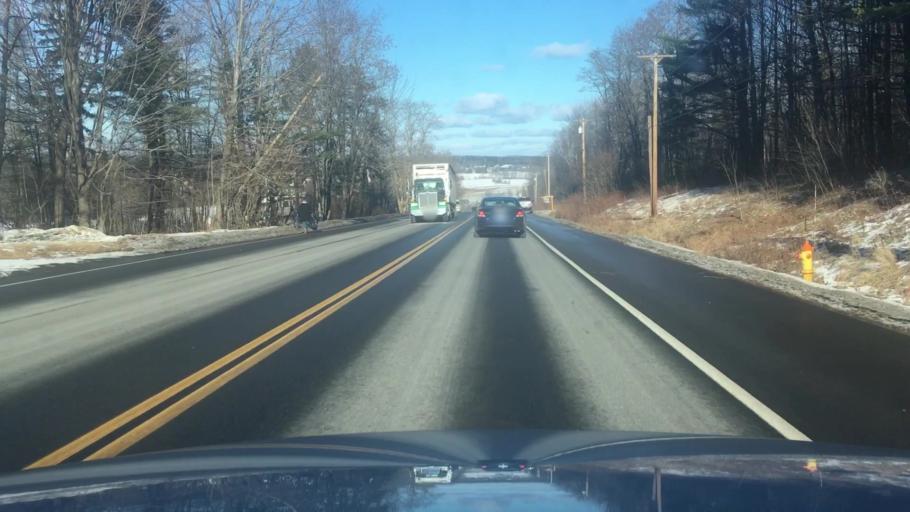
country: US
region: Maine
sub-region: Kennebec County
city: Waterville
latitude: 44.5922
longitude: -69.6531
